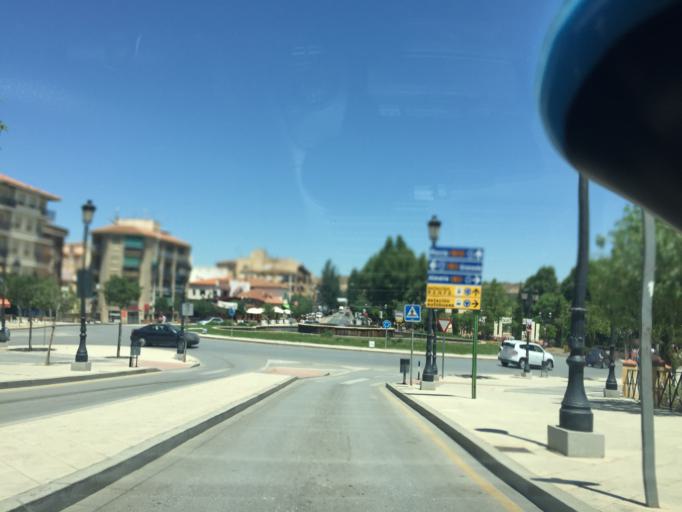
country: ES
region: Andalusia
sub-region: Provincia de Granada
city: Guadix
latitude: 37.3023
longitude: -3.1357
